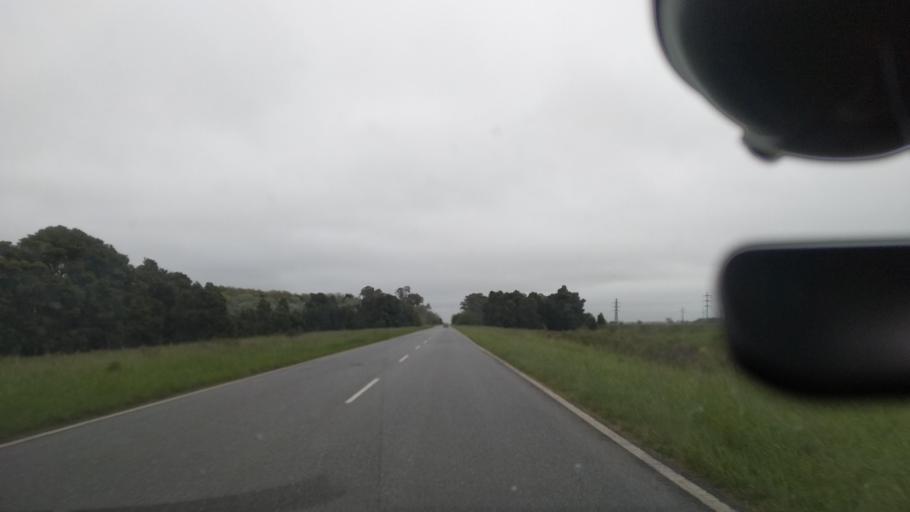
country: AR
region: Buenos Aires
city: Veronica
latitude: -35.3128
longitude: -57.4878
